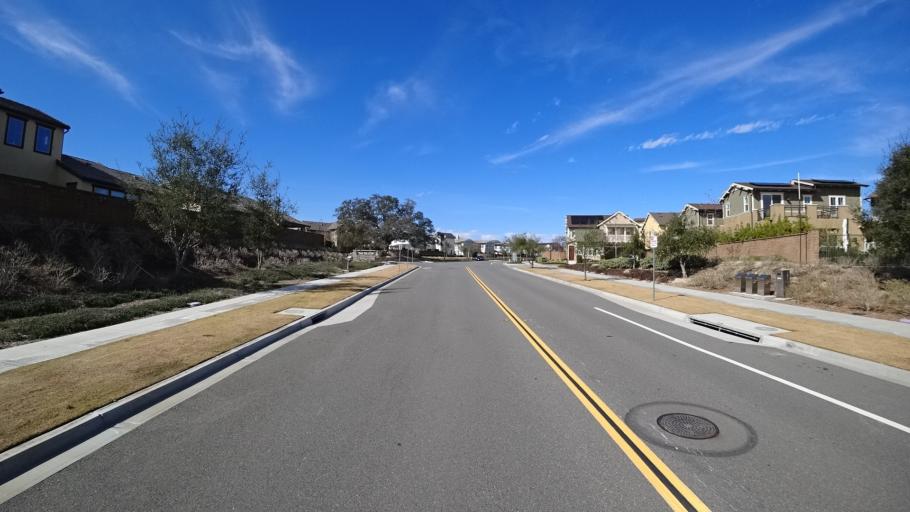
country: US
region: California
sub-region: Orange County
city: Ladera Ranch
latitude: 33.5402
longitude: -117.5986
